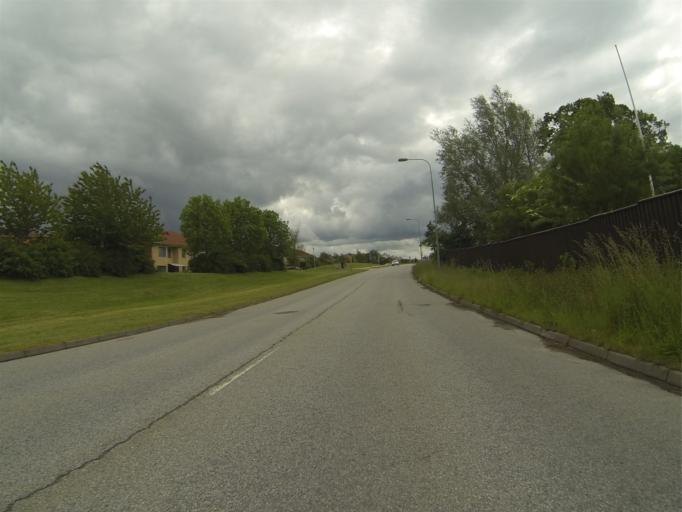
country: SE
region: Skane
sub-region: Lunds Kommun
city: Genarp
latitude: 55.6639
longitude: 13.3589
